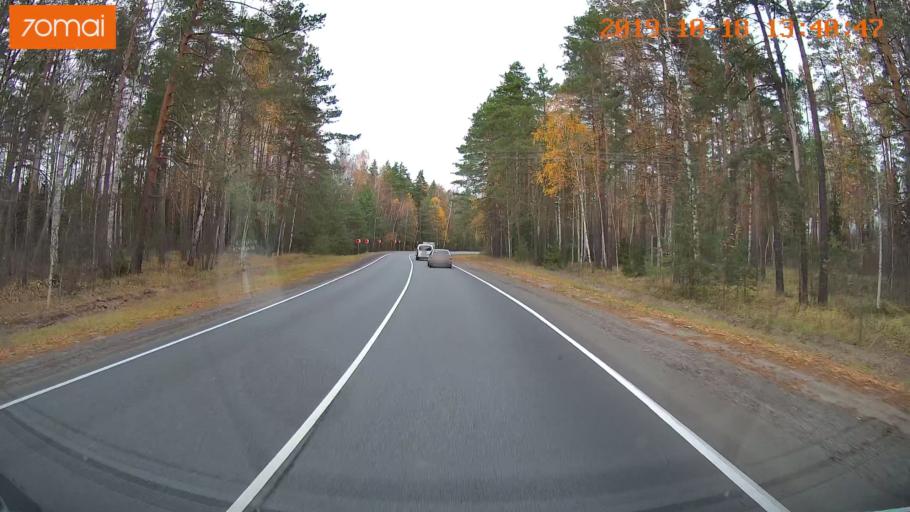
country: RU
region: Rjazan
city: Solotcha
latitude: 54.9139
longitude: 39.9978
